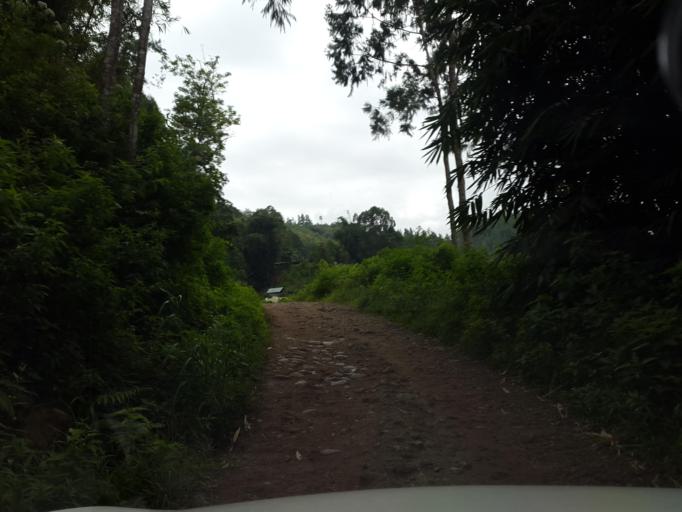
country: ID
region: South Sulawesi
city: Rantepang
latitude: -2.8669
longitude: 119.9487
